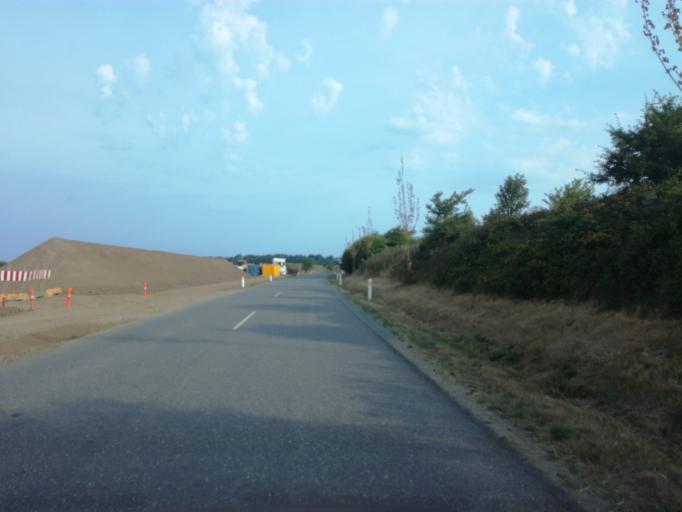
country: DK
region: South Denmark
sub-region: Vejle Kommune
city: Borkop
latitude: 55.6399
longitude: 9.6383
